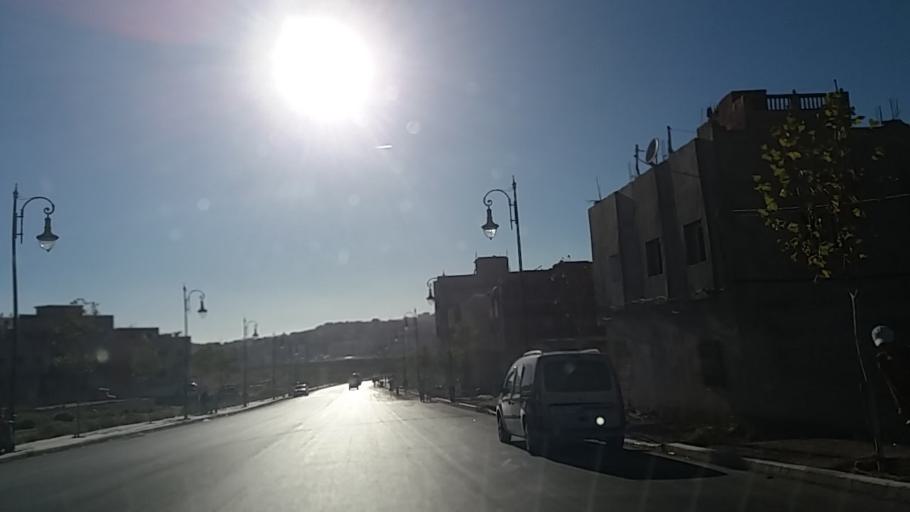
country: MA
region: Tanger-Tetouan
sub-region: Tanger-Assilah
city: Tangier
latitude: 35.7291
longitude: -5.7926
